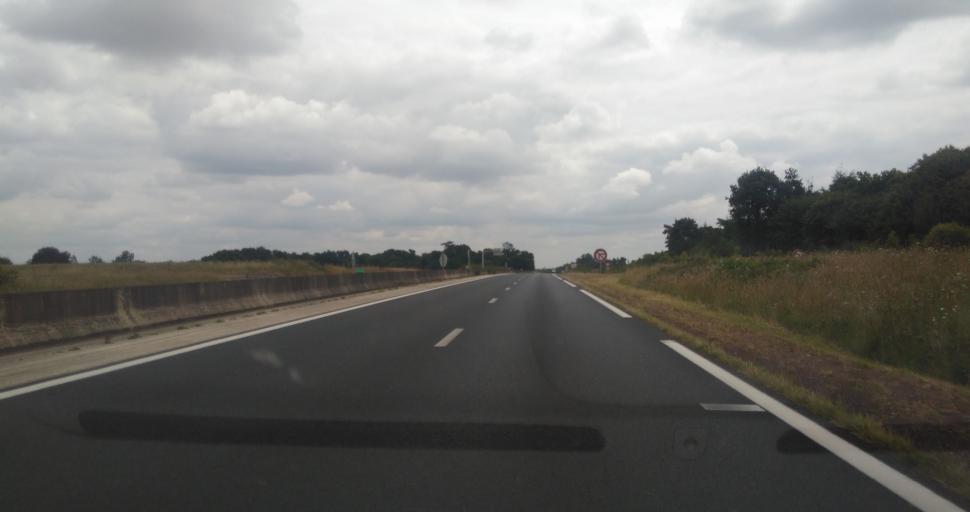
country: FR
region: Pays de la Loire
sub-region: Departement de la Vendee
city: Bournezeau
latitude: 46.6442
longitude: -1.2007
